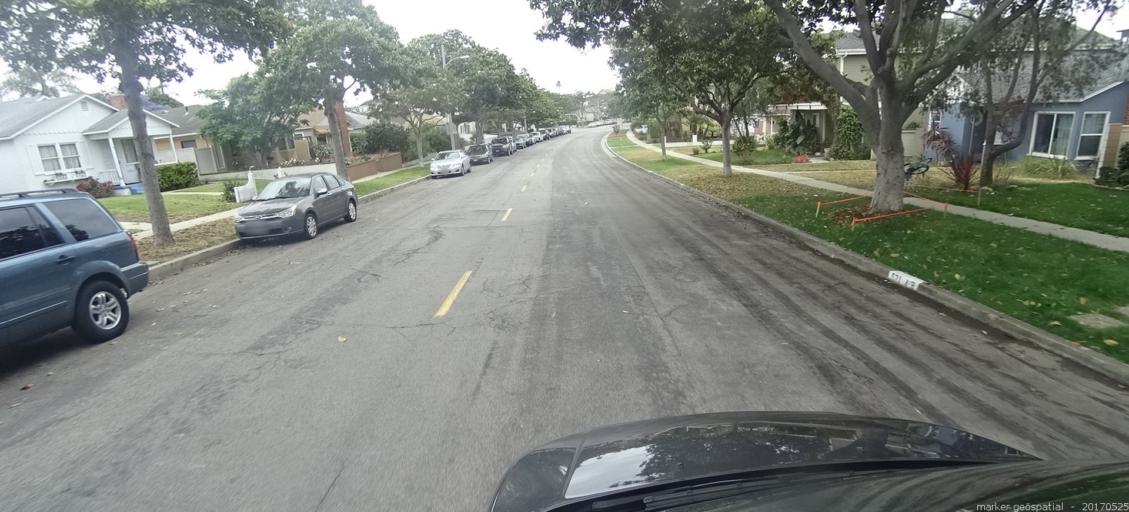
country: US
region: California
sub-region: Los Angeles County
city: Redondo Beach
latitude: 33.8513
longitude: -118.3818
